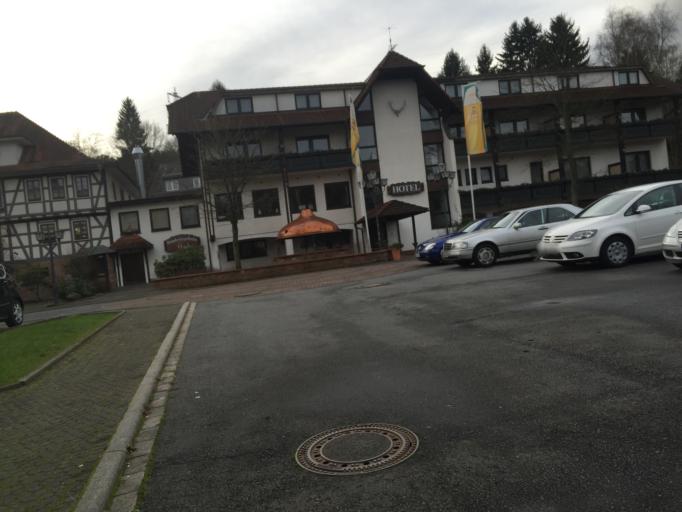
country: DE
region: Hesse
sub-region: Regierungsbezirk Darmstadt
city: Erbach
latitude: 49.6738
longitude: 8.9243
